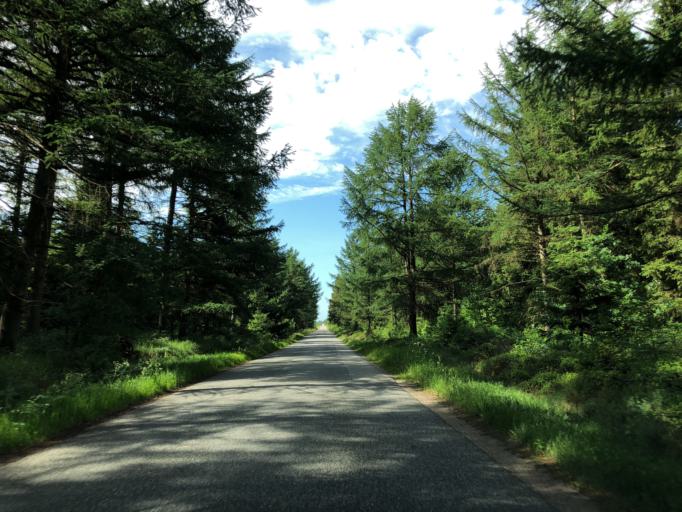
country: DK
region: Central Jutland
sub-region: Herning Kommune
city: Lind
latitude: 56.0436
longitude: 8.9332
